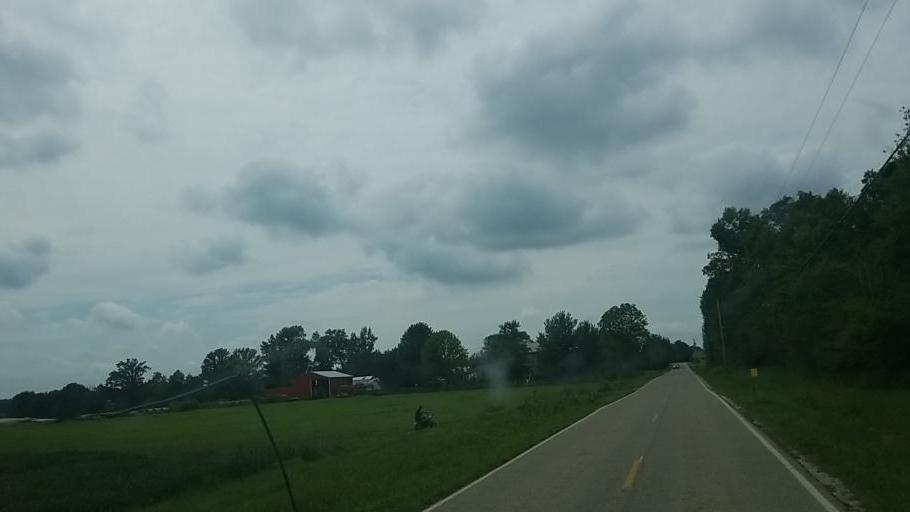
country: US
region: Ohio
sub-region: Fairfield County
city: Lithopolis
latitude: 39.7534
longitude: -82.8725
